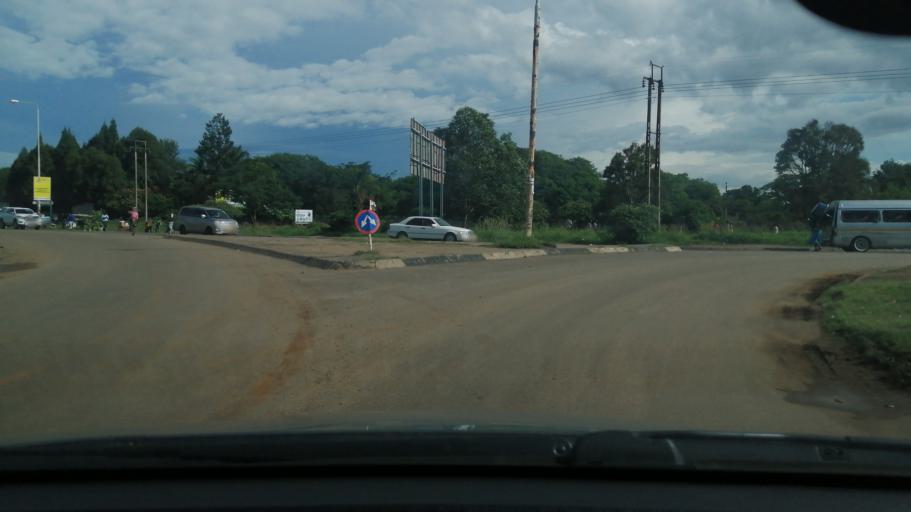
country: ZW
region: Harare
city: Harare
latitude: -17.7617
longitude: 30.9805
